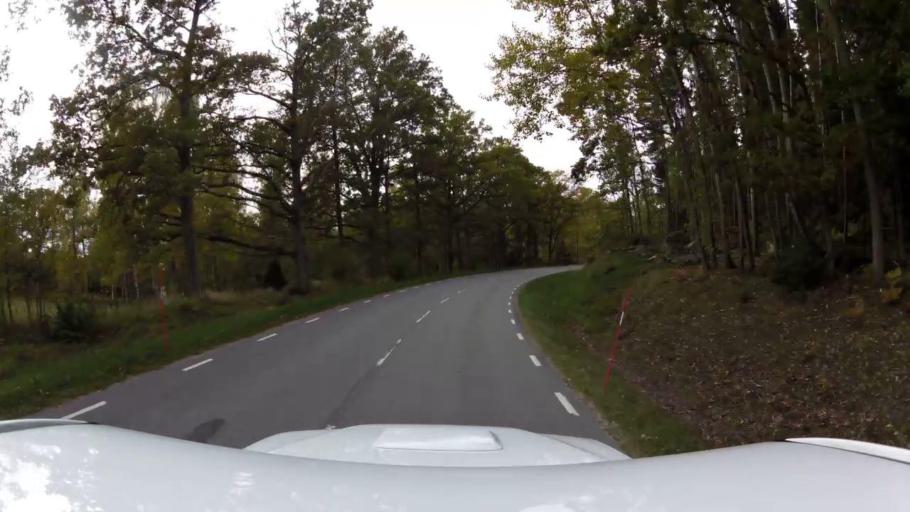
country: SE
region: OEstergoetland
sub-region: Linkopings Kommun
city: Ekangen
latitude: 58.5412
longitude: 15.6334
